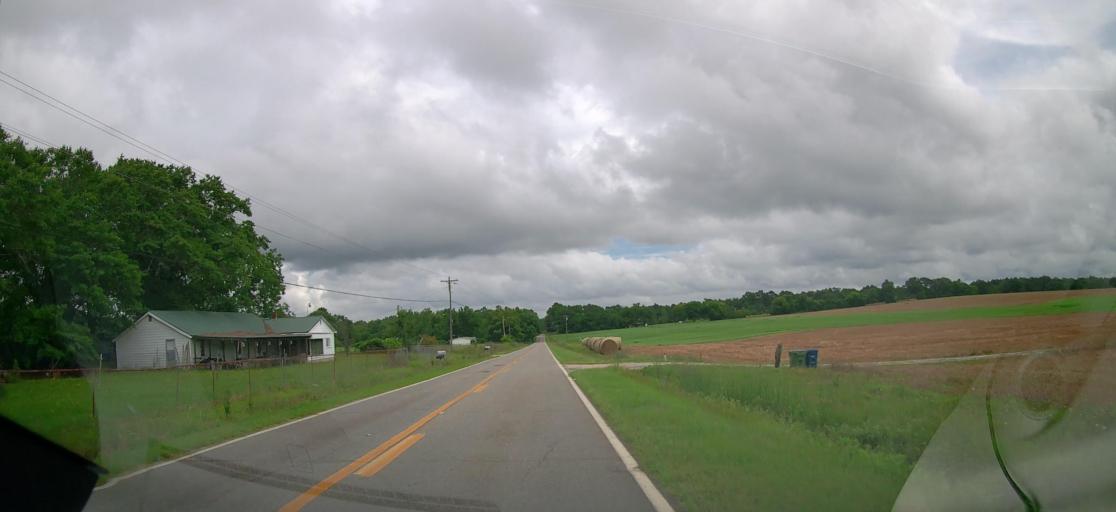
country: US
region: Georgia
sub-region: Bibb County
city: West Point
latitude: 32.7361
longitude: -83.7658
